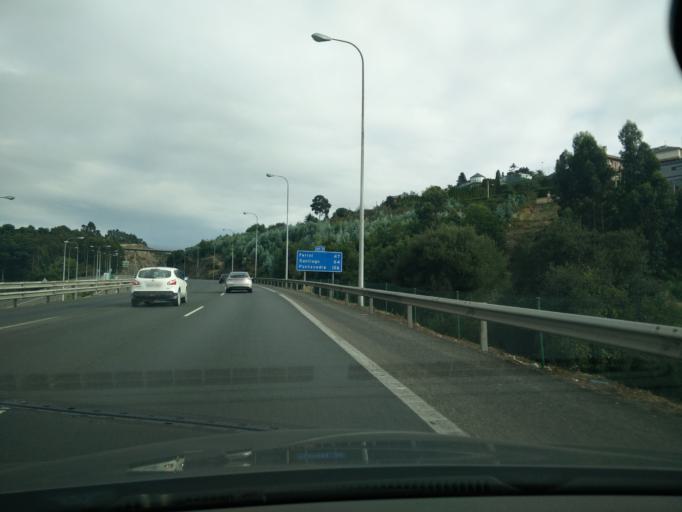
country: ES
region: Galicia
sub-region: Provincia da Coruna
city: Culleredo
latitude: 43.3285
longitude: -8.3968
